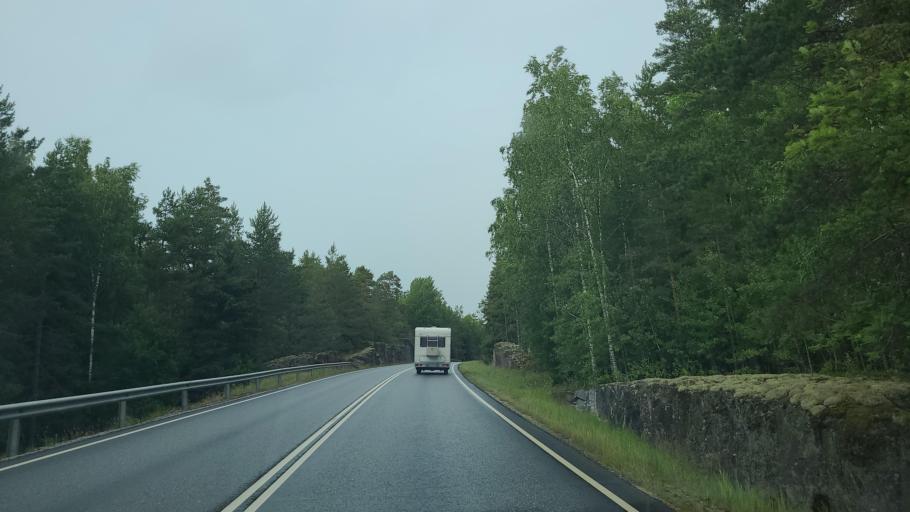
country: FI
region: Varsinais-Suomi
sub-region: Turku
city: Sauvo
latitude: 60.2795
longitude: 22.6687
